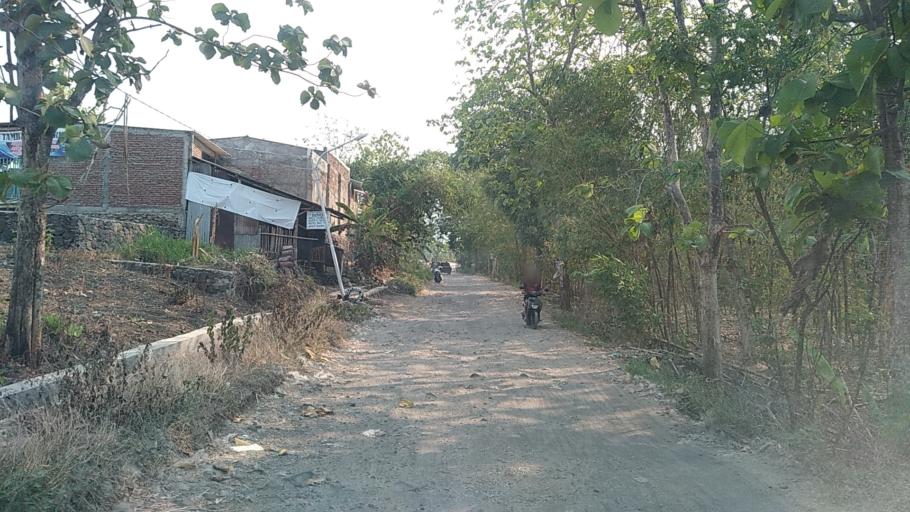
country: ID
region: Central Java
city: Mranggen
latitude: -7.0686
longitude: 110.4735
